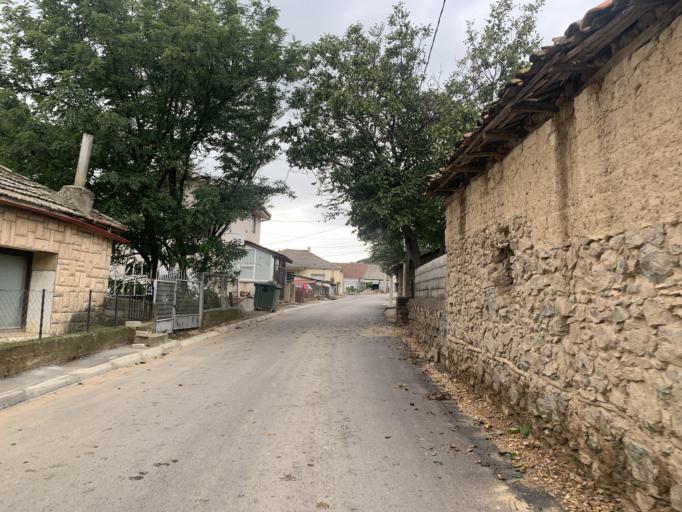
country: MK
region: Bogdanci
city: Bogdanci
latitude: 41.1923
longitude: 22.5376
